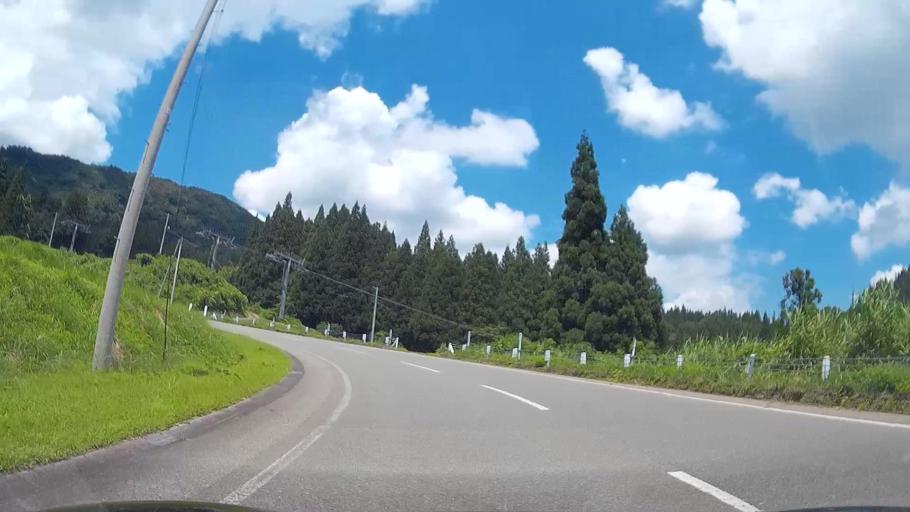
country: JP
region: Niigata
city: Shiozawa
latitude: 37.0244
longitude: 138.8046
